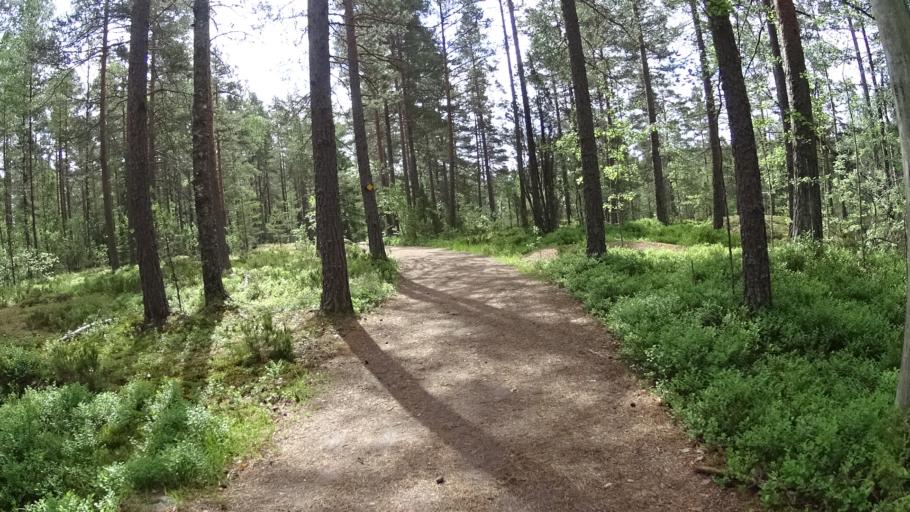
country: FI
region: Uusimaa
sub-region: Helsinki
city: Espoo
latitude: 60.2950
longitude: 24.5187
